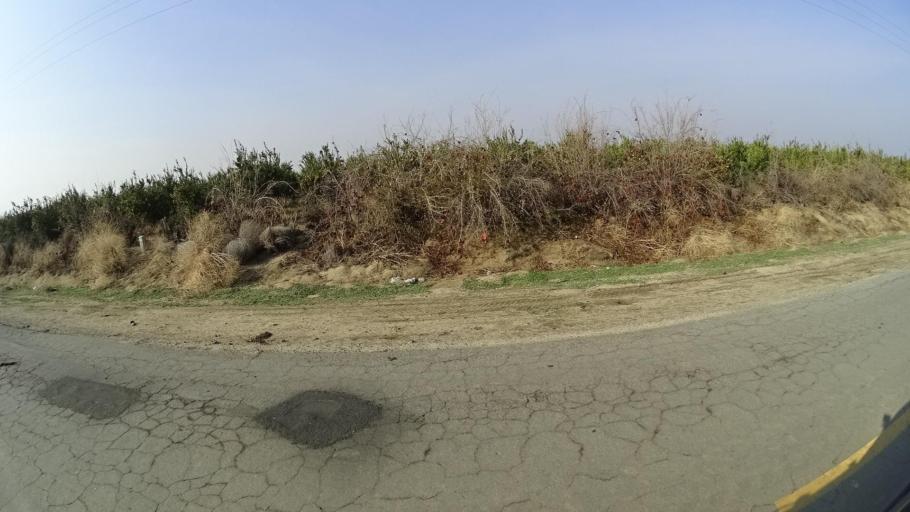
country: US
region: California
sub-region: Kern County
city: Lebec
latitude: 35.0249
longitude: -118.8466
